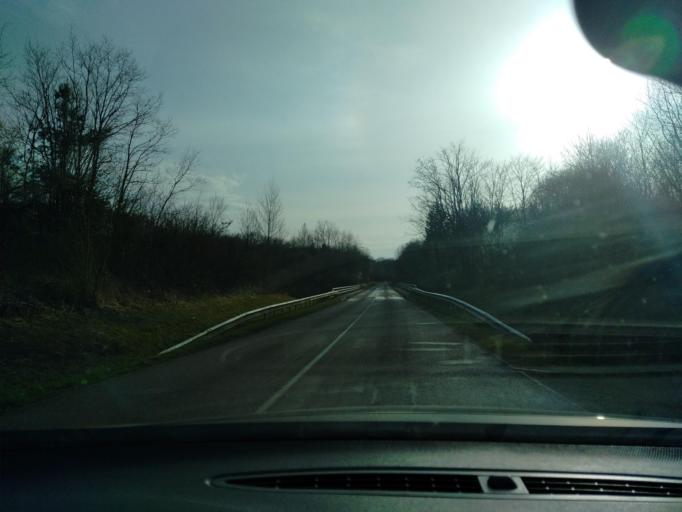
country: FR
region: Franche-Comte
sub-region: Departement du Jura
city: Choisey
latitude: 47.0061
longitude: 5.4891
